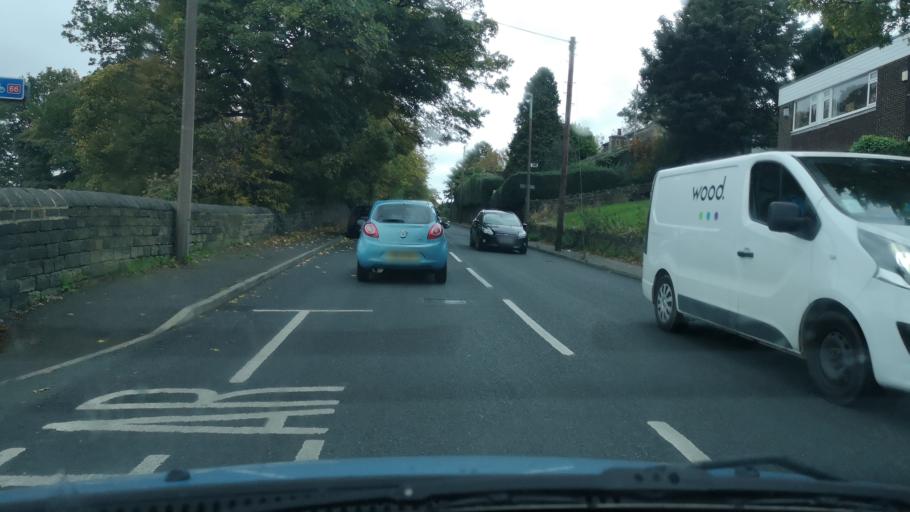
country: GB
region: England
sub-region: Kirklees
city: Heckmondwike
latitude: 53.6965
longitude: -1.6591
